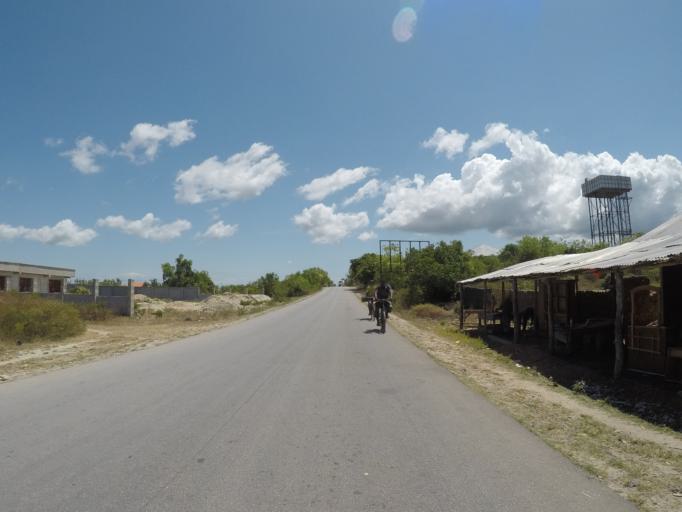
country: TZ
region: Zanzibar Central/South
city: Nganane
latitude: -6.2667
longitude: 39.5303
